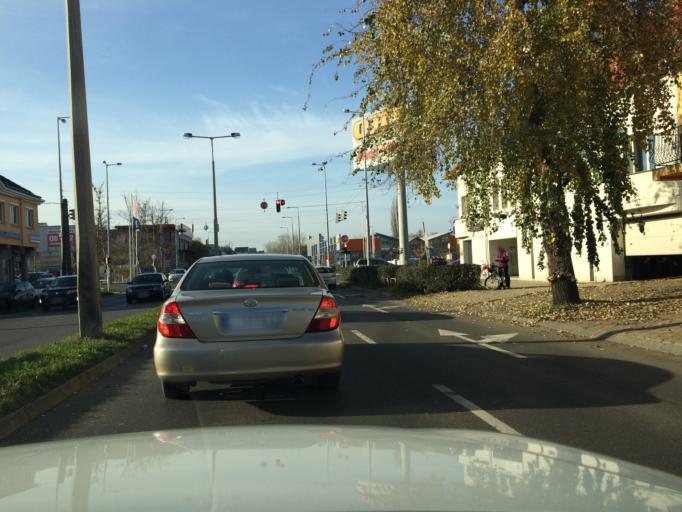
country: HU
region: Szabolcs-Szatmar-Bereg
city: Nyiregyhaza
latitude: 47.9563
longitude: 21.7292
